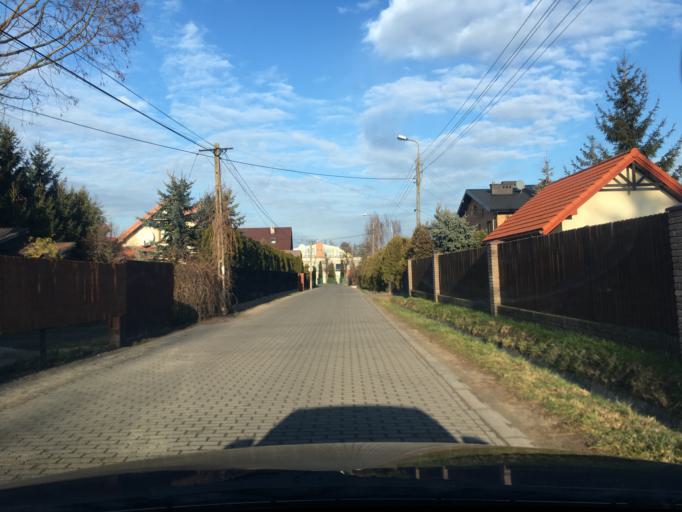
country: PL
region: Masovian Voivodeship
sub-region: Powiat piaseczynski
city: Lesznowola
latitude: 52.0358
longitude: 20.9419
